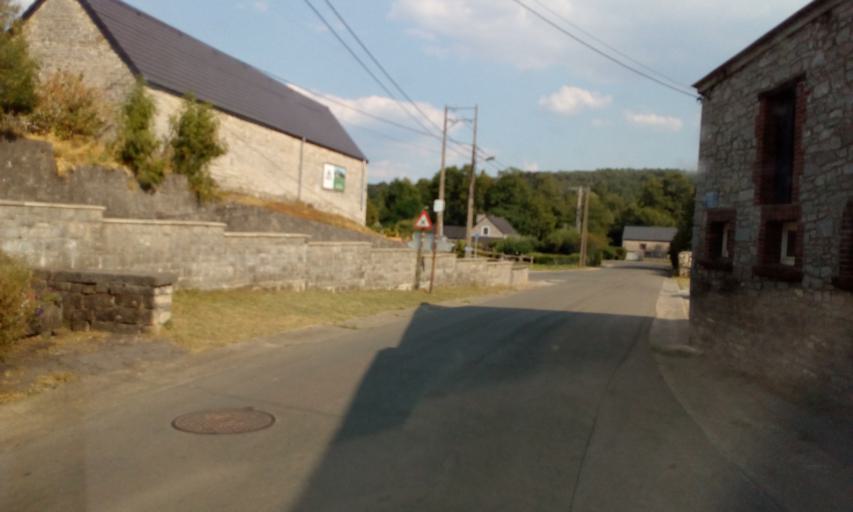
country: BE
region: Wallonia
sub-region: Province du Luxembourg
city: Tellin
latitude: 50.1073
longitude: 5.1922
